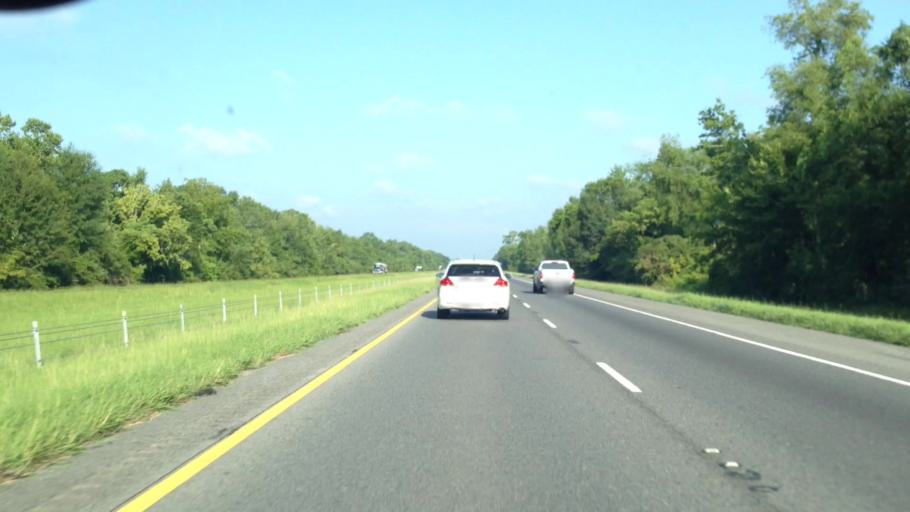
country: US
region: Louisiana
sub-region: Ascension Parish
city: Sorrento
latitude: 30.1501
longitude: -90.7839
